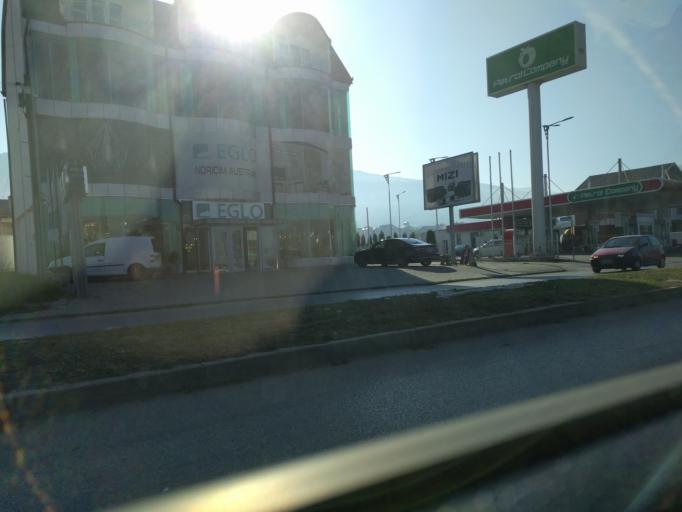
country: XK
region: Prizren
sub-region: Prizren
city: Prizren
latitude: 42.2368
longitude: 20.7606
